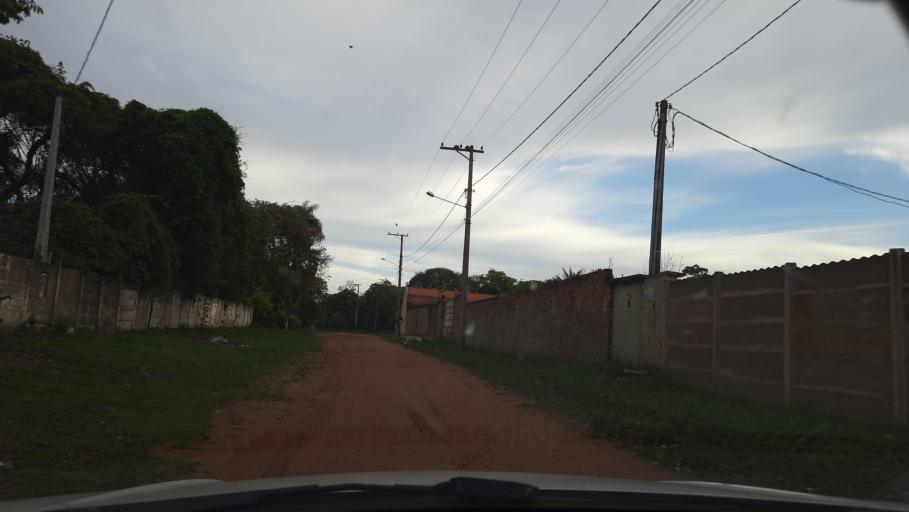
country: BR
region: Sao Paulo
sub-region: Casa Branca
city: Casa Branca
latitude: -21.7773
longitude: -47.0655
